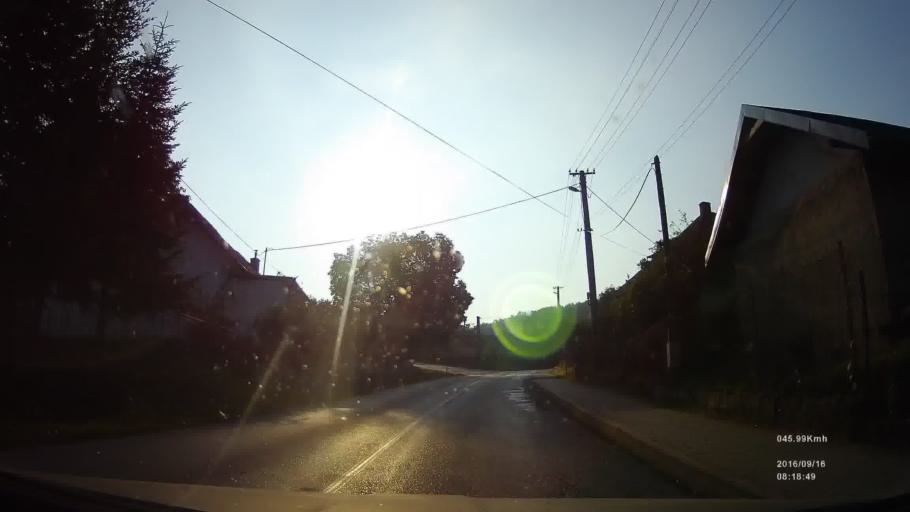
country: SK
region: Presovsky
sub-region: Okres Presov
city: Presov
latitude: 48.8631
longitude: 21.2372
